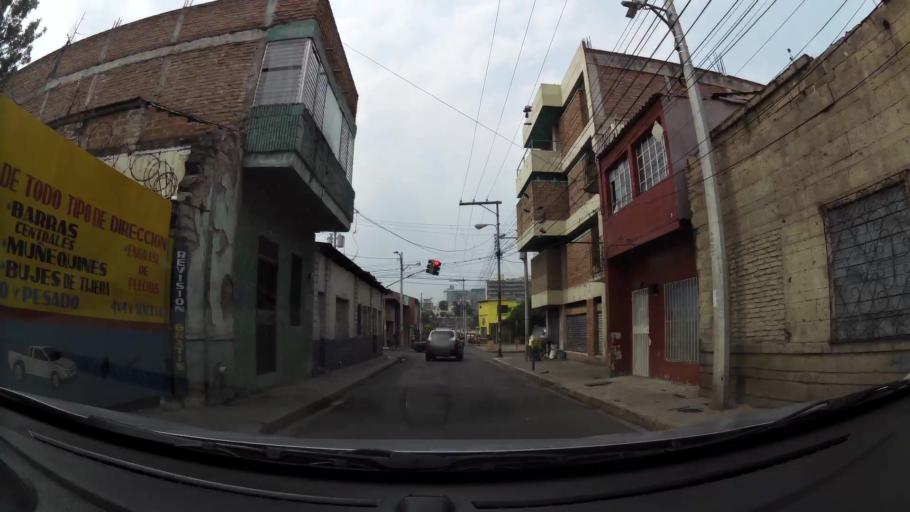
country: HN
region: Francisco Morazan
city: Tegucigalpa
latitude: 14.1003
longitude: -87.2062
